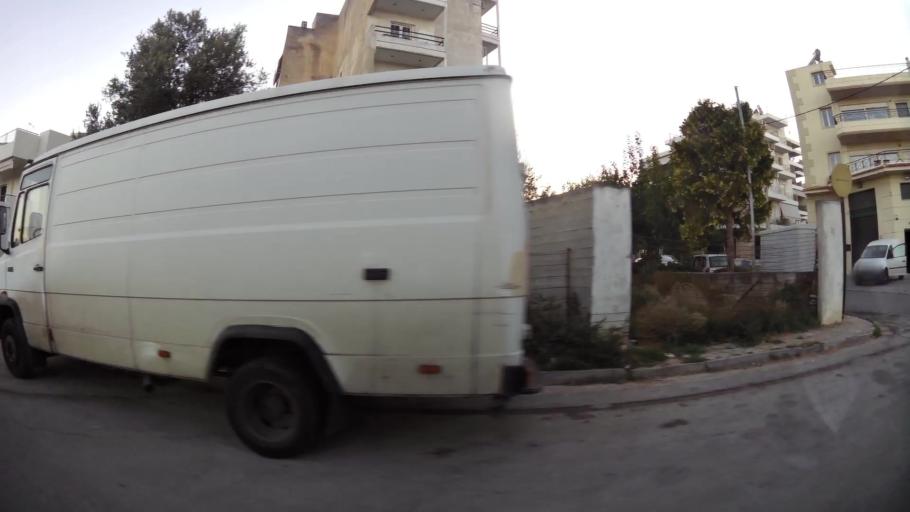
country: GR
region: Attica
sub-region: Nomarchia Anatolikis Attikis
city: Spata
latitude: 37.9628
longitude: 23.9248
